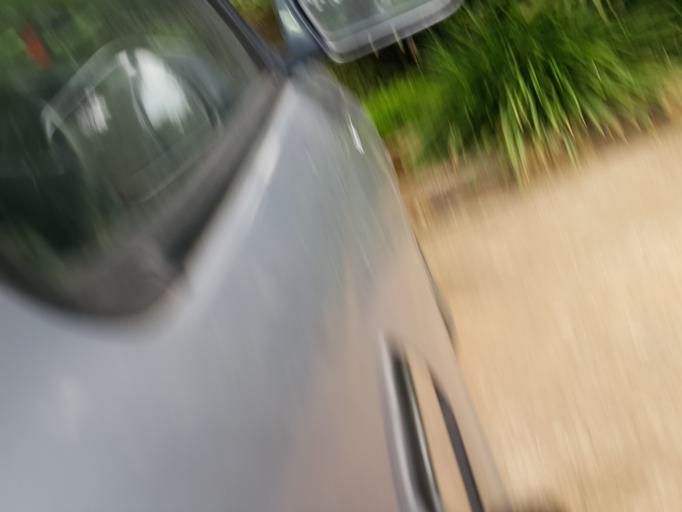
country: TH
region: Mae Hong Son
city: Mae Hong Son
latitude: 19.4909
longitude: 97.9576
